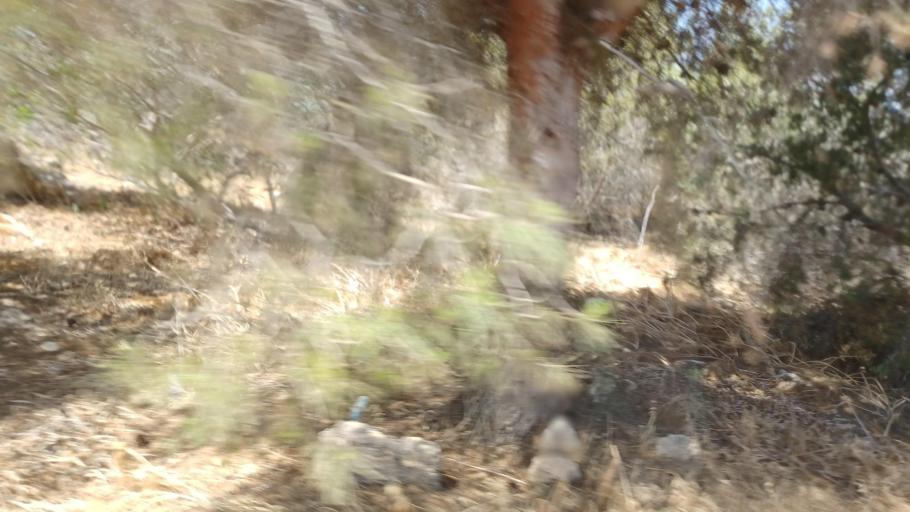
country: CY
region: Ammochostos
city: Paralimni
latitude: 35.0040
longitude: 33.9601
